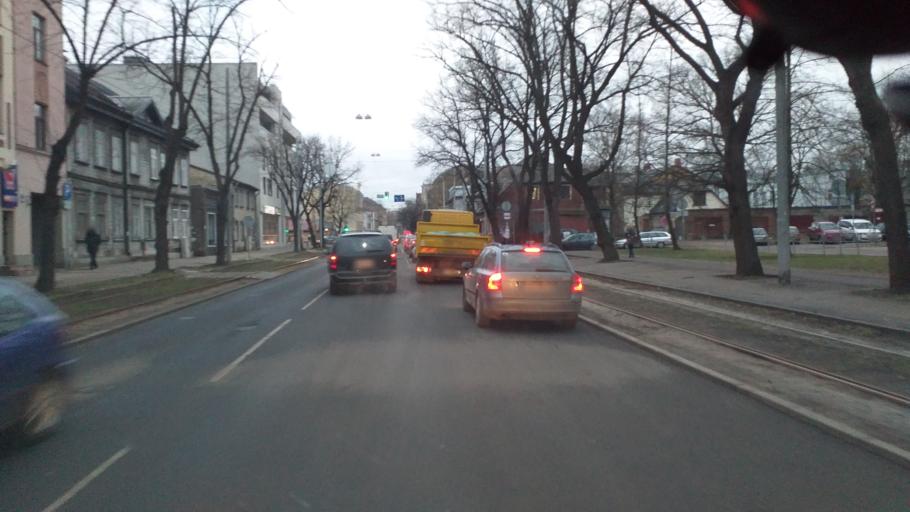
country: LV
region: Riga
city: Riga
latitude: 56.9664
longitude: 24.1339
